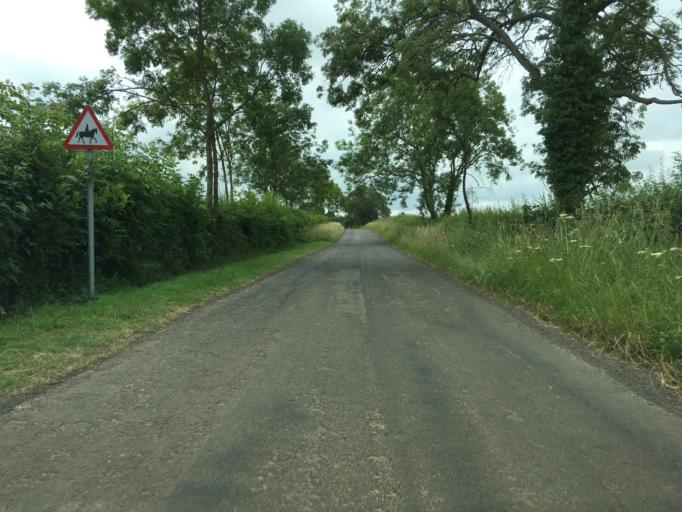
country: GB
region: England
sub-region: Oxfordshire
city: Bloxham
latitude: 51.9586
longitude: -1.3902
